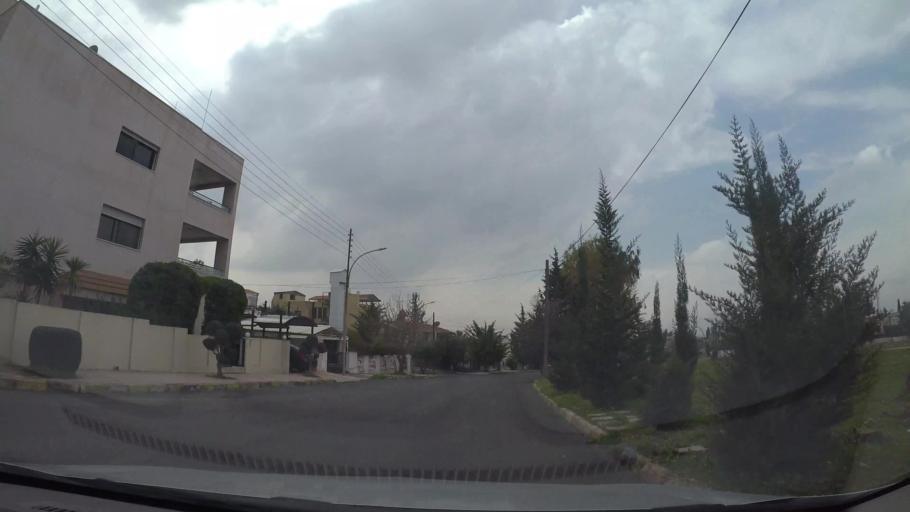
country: JO
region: Amman
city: Umm as Summaq
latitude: 31.8932
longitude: 35.8583
